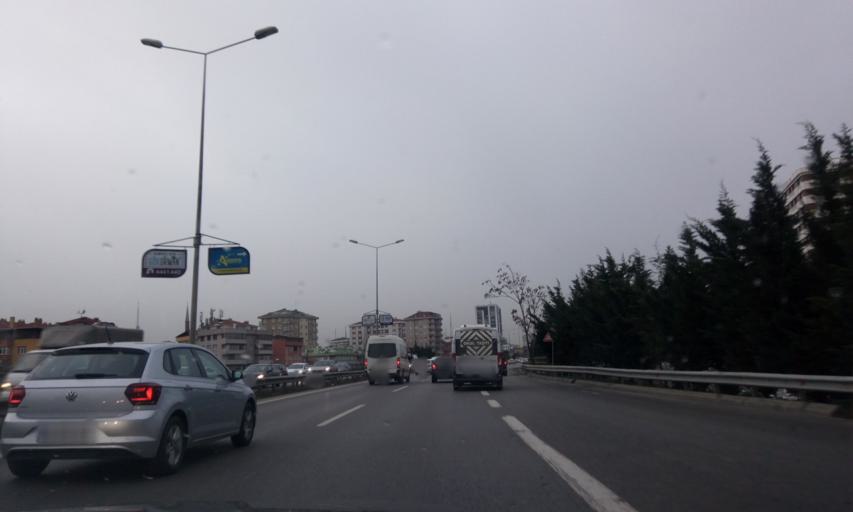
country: TR
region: Istanbul
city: Umraniye
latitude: 41.0290
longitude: 29.1068
